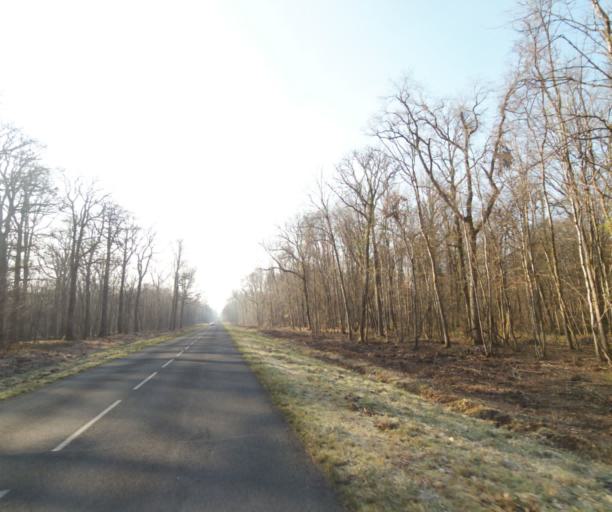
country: FR
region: Champagne-Ardenne
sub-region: Departement de la Haute-Marne
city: Wassy
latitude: 48.4778
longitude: 4.9298
